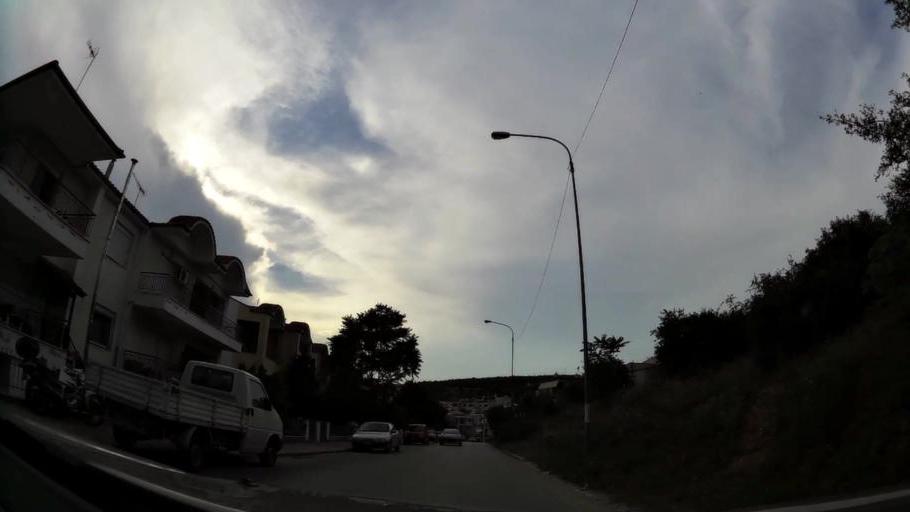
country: GR
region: Central Macedonia
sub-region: Nomos Thessalonikis
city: Pefka
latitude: 40.6612
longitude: 22.9902
